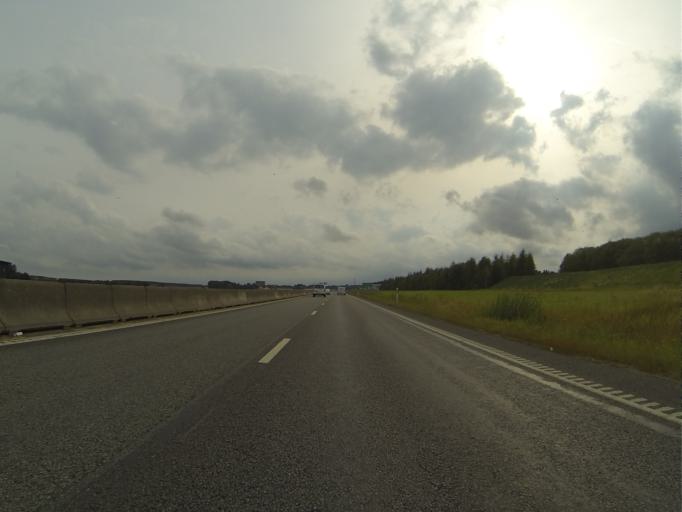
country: SE
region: Skane
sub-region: Kristianstads Kommun
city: Kristianstad
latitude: 56.0121
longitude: 14.1131
